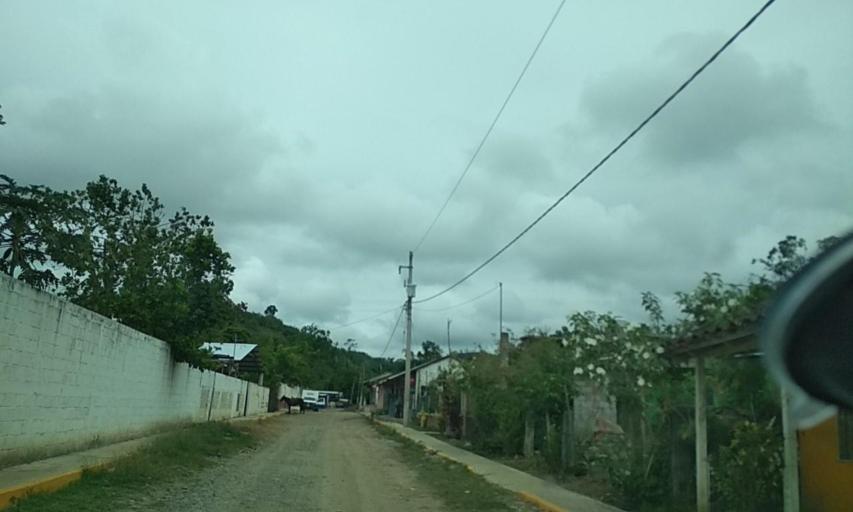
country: MX
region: Veracruz
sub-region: Papantla
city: Residencial Tajin
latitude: 20.6014
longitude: -97.3348
